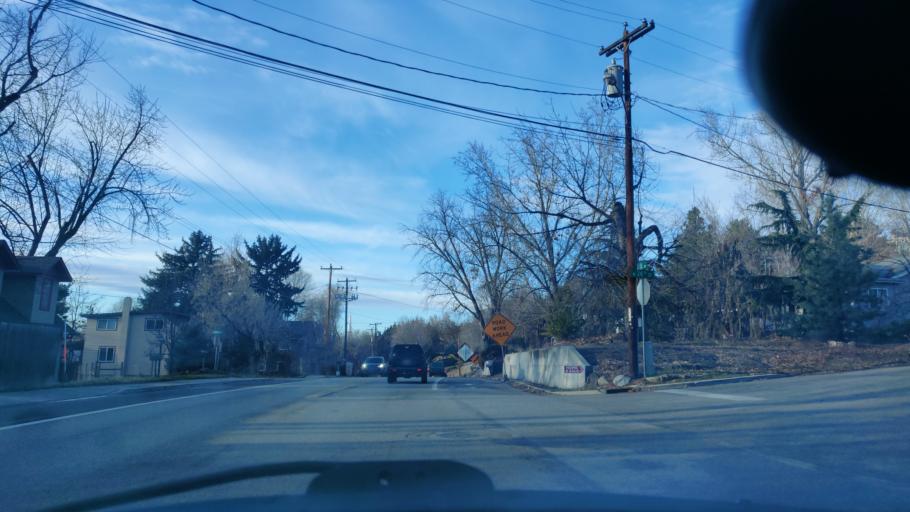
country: US
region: Idaho
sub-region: Ada County
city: Garden City
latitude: 43.6460
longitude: -116.2183
